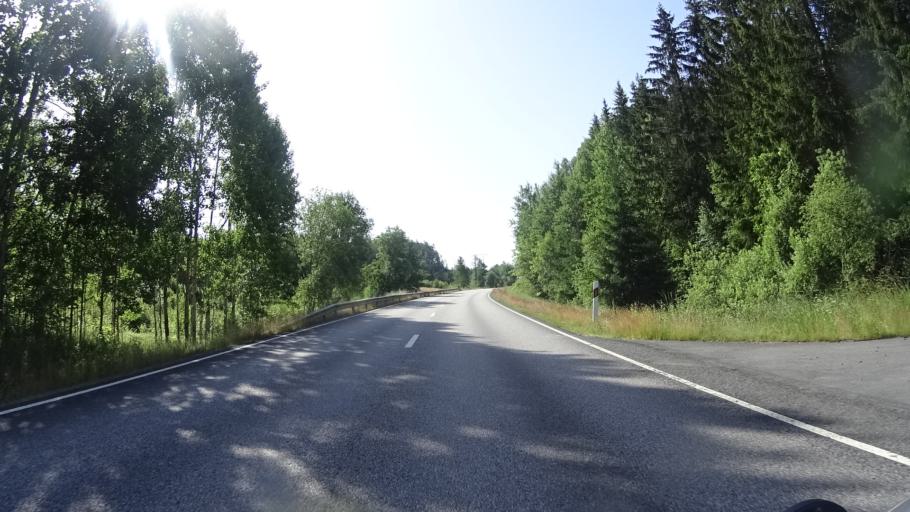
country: SE
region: Kalmar
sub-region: Vasterviks Kommun
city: Overum
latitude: 58.0499
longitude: 16.2076
